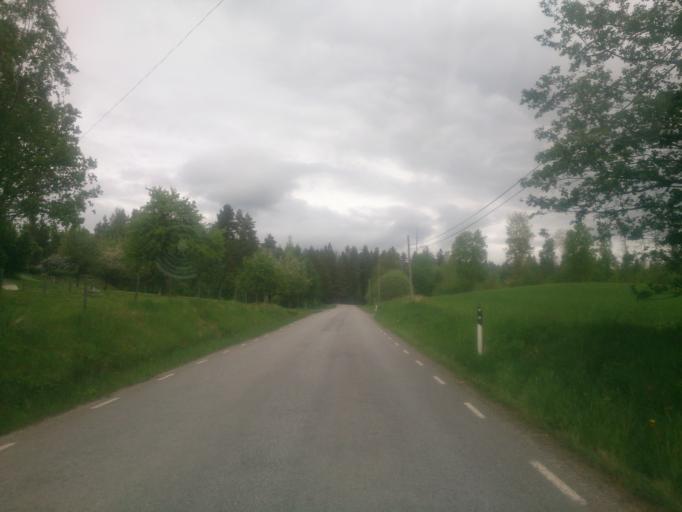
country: SE
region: OEstergoetland
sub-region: Atvidabergs Kommun
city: Atvidaberg
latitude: 58.2217
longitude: 16.0504
